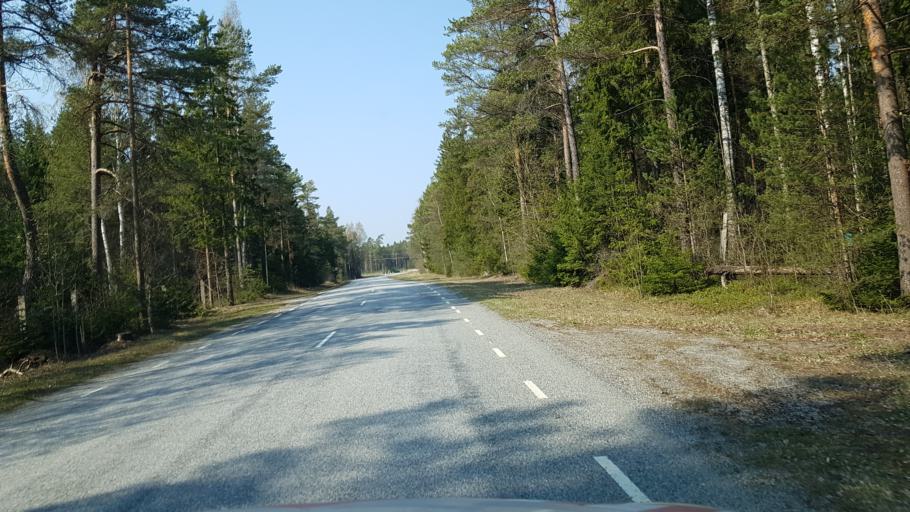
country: EE
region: Harju
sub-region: Paldiski linn
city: Paldiski
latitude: 59.2496
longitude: 23.9184
